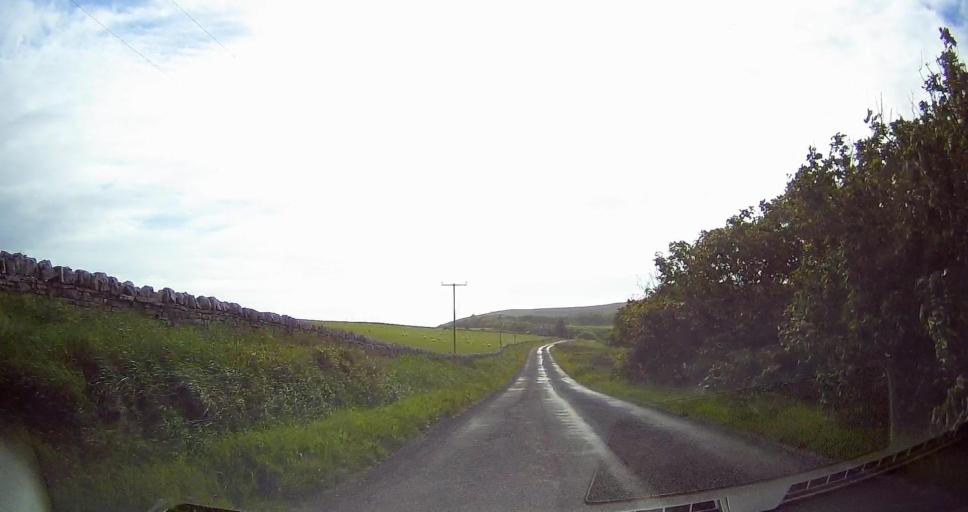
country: GB
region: Scotland
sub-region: Orkney Islands
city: Stromness
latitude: 58.7855
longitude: -3.2500
